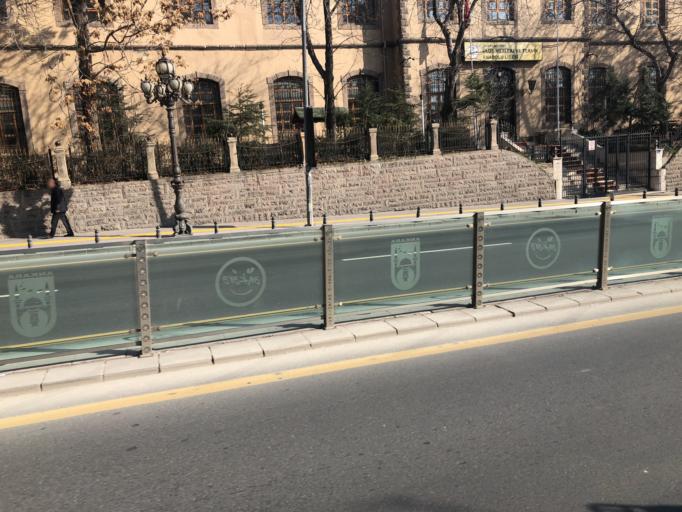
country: TR
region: Ankara
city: Ankara
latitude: 39.9399
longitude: 32.8543
